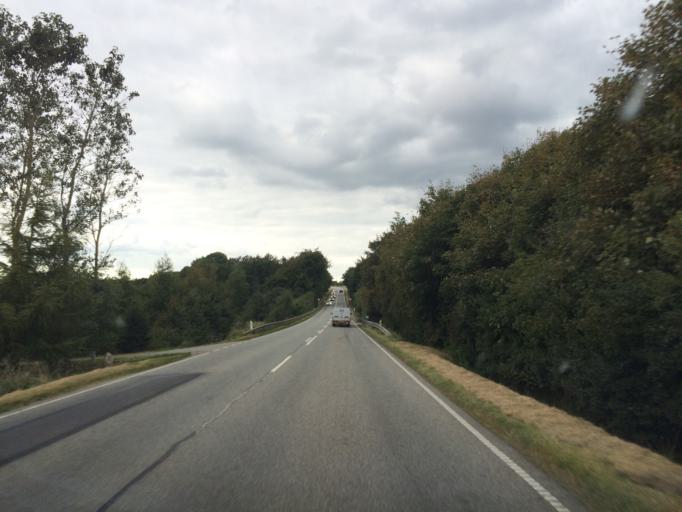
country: DK
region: Central Jutland
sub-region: Ringkobing-Skjern Kommune
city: Ringkobing
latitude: 56.0673
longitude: 8.3817
